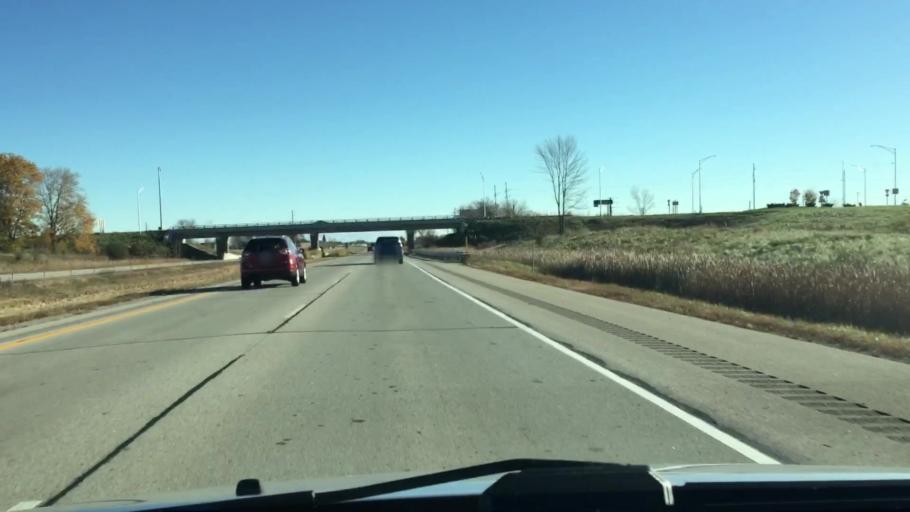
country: US
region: Wisconsin
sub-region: Outagamie County
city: Kaukauna
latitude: 44.3049
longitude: -88.2517
